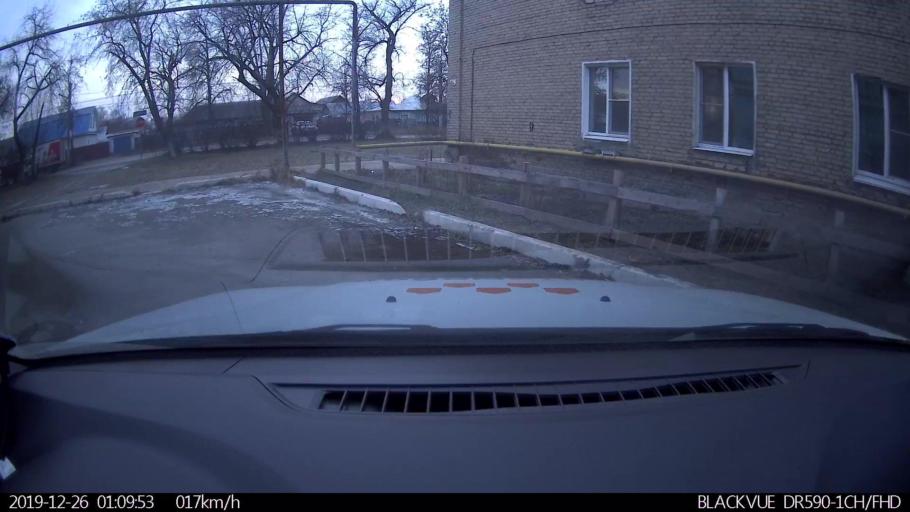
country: RU
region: Nizjnij Novgorod
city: Nizhniy Novgorod
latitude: 56.2879
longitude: 43.9131
